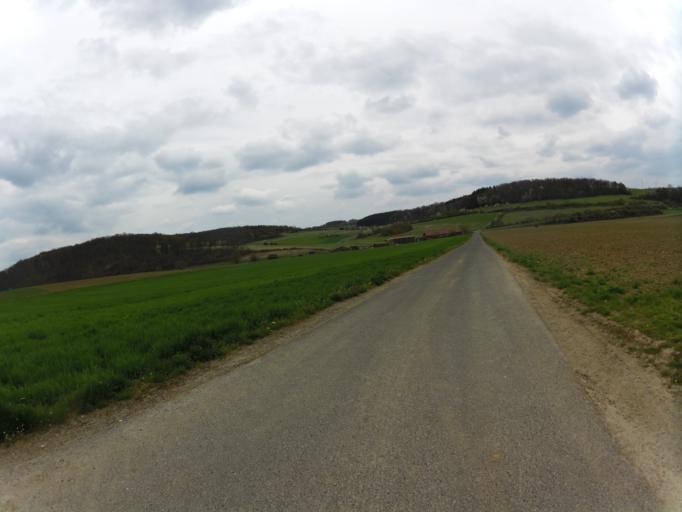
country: DE
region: Bavaria
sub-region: Regierungsbezirk Unterfranken
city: Greussenheim
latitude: 49.8201
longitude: 9.7702
